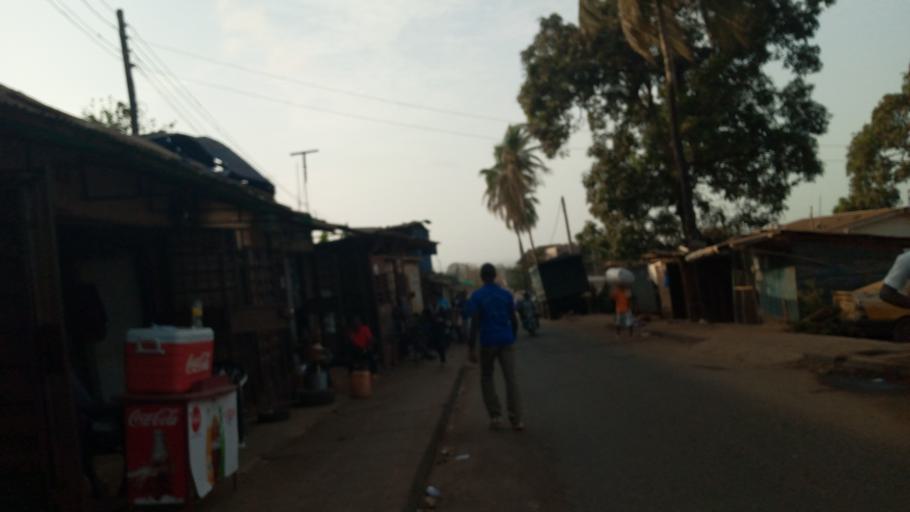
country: SL
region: Western Area
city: Freetown
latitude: 8.4709
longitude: -13.2427
